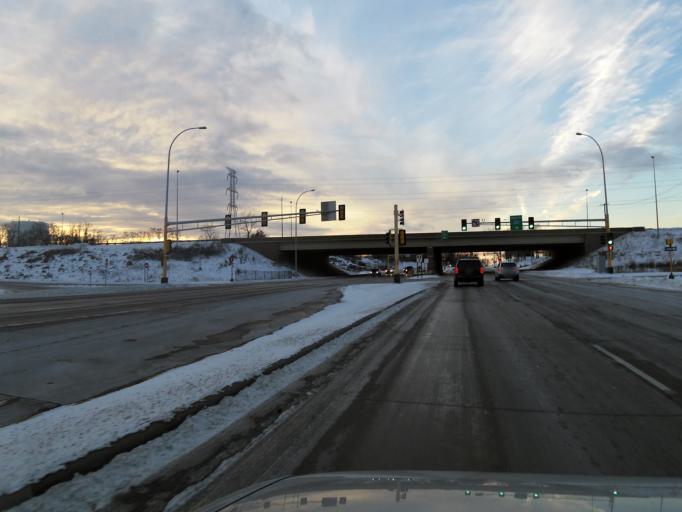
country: US
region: Minnesota
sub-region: Hennepin County
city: Hopkins
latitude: 44.8915
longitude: -93.4419
